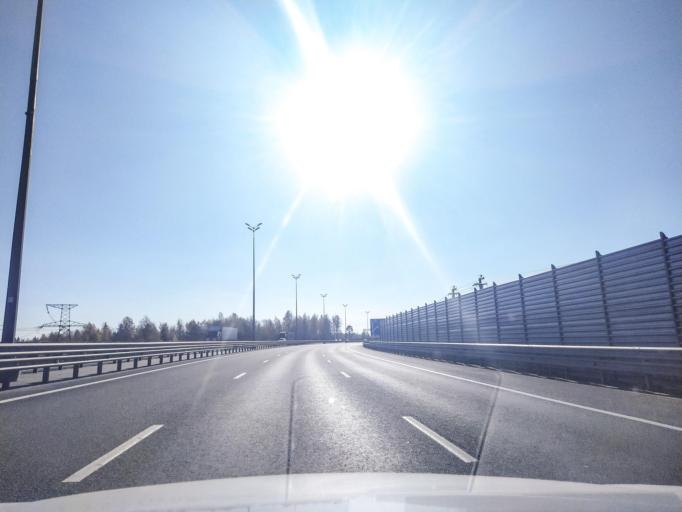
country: RU
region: Leningrad
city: Maloye Verevo
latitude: 59.5866
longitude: 30.1808
